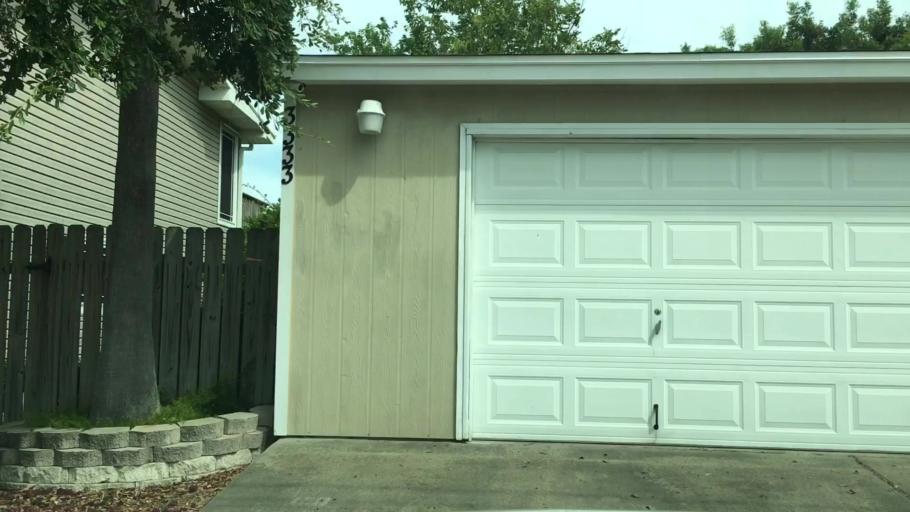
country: US
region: Texas
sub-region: Nueces County
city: Corpus Christi
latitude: 27.6264
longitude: -97.2932
